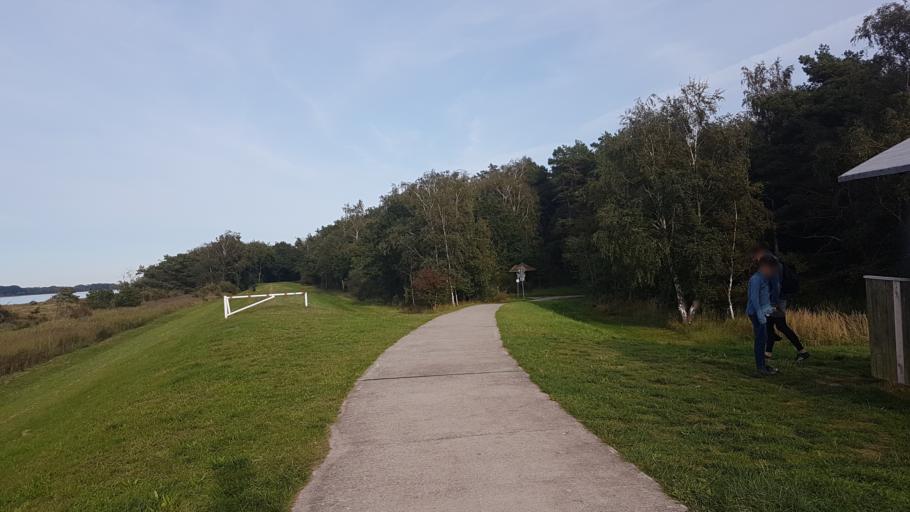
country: DE
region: Mecklenburg-Vorpommern
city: Hiddensee
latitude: 54.4885
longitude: 13.1618
